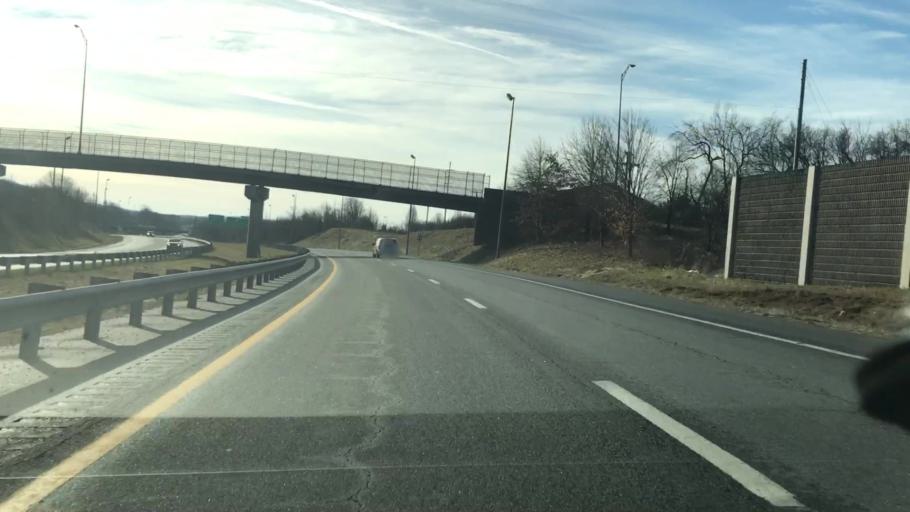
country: US
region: Virginia
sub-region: Montgomery County
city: Merrimac
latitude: 37.1714
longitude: -80.4172
